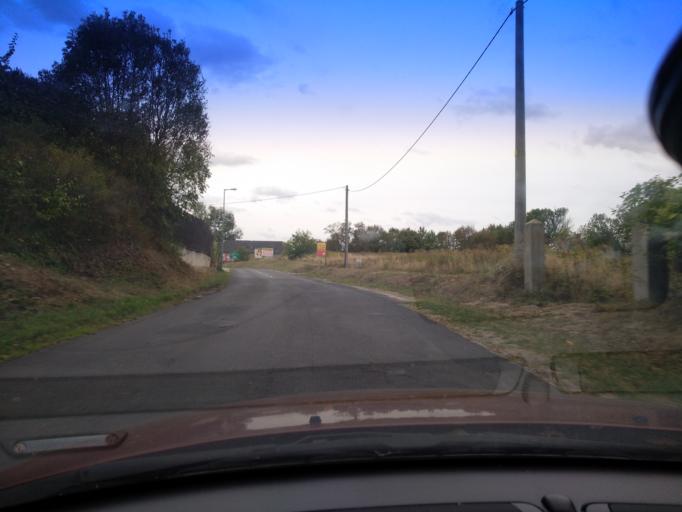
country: DE
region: Saxony
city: Goerlitz
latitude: 51.1620
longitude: 14.9978
